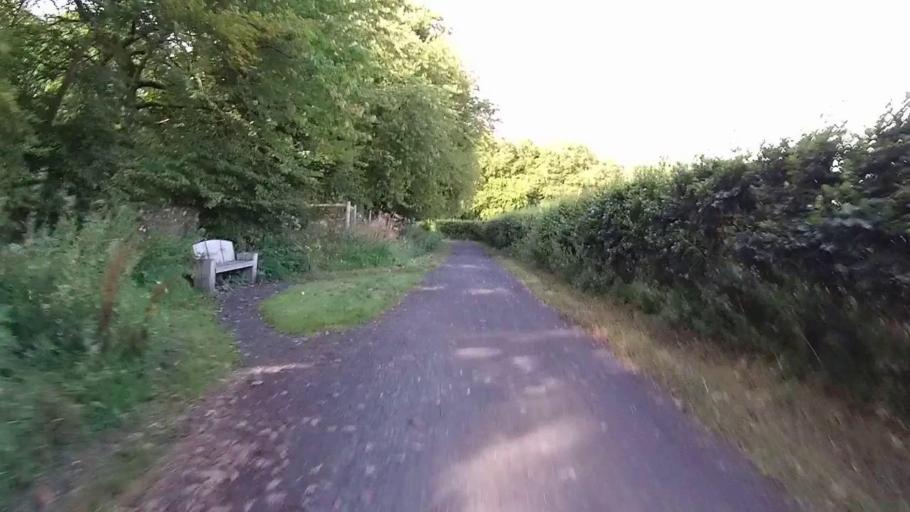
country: GB
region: Scotland
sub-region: Perth and Kinross
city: Kinross
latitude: 56.2035
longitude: -3.4064
